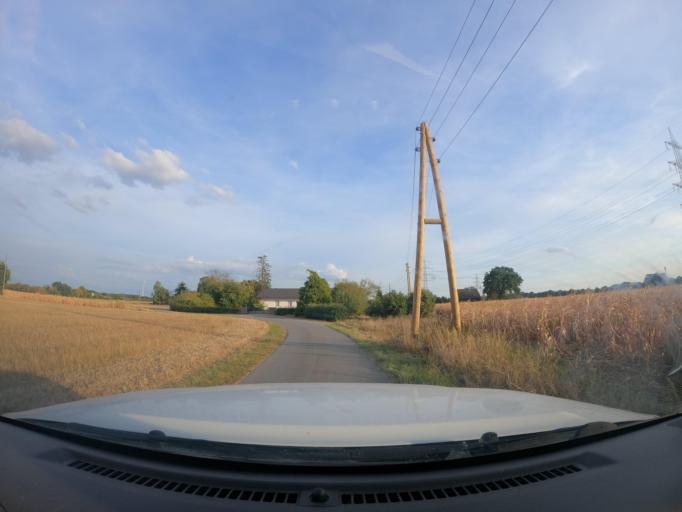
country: DE
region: North Rhine-Westphalia
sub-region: Regierungsbezirk Dusseldorf
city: Hamminkeln
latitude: 51.7156
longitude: 6.5826
